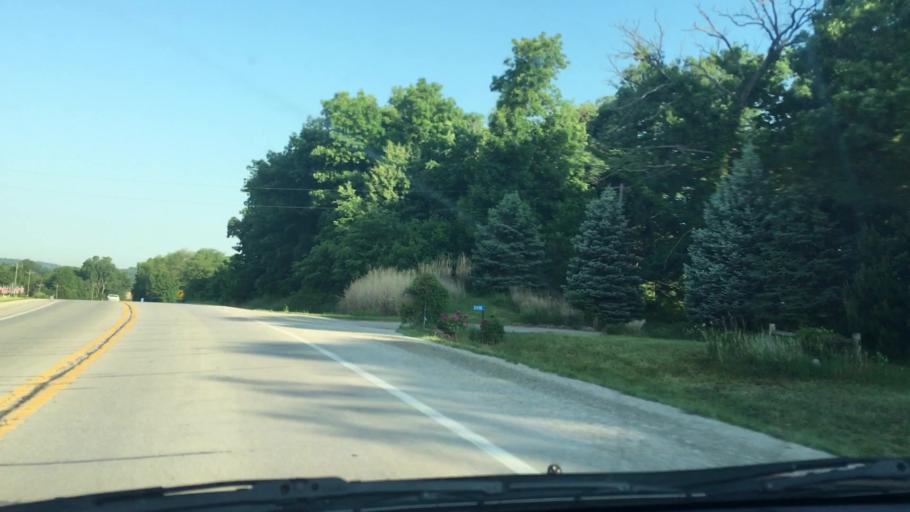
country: US
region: Iowa
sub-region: Johnson County
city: Tiffin
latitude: 41.7112
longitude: -91.6929
